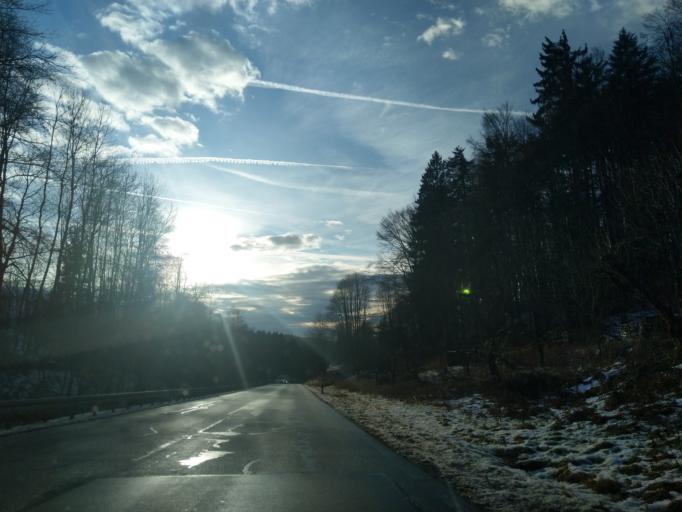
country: DE
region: Bavaria
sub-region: Lower Bavaria
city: Schaufling
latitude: 48.8664
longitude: 13.0343
